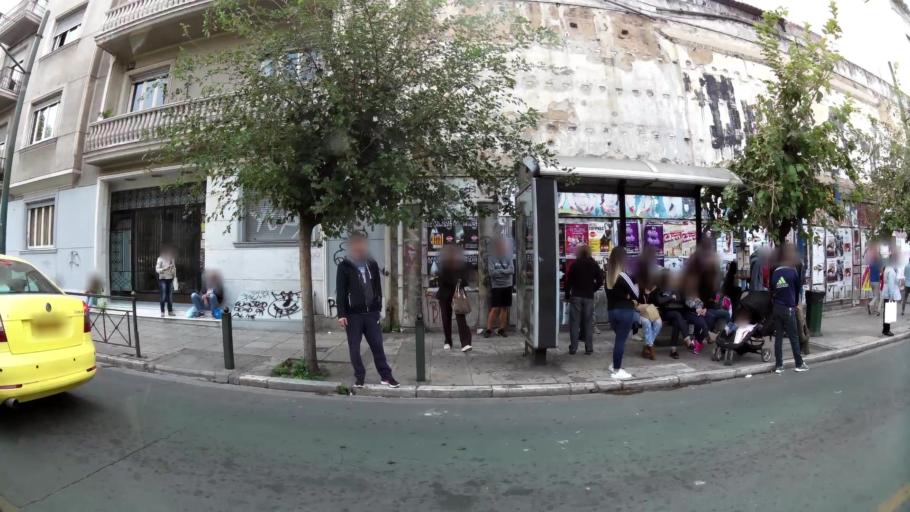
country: GR
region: Attica
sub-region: Nomarchia Athinas
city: Kipseli
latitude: 37.9913
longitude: 23.7339
